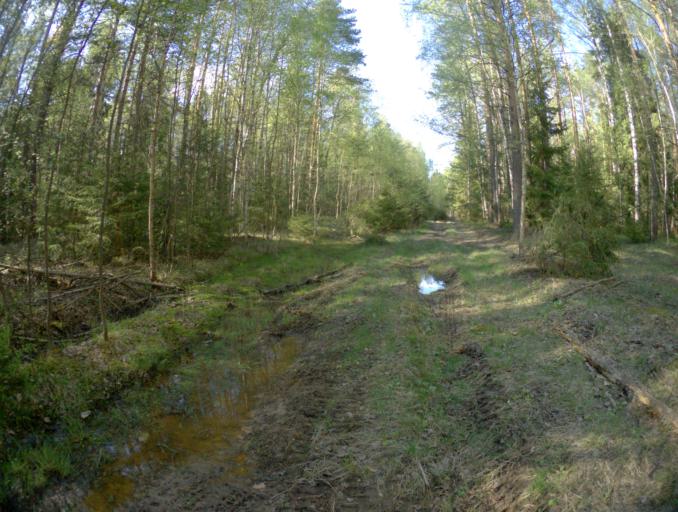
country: RU
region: Vladimir
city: Golovino
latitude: 55.9170
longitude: 40.4399
